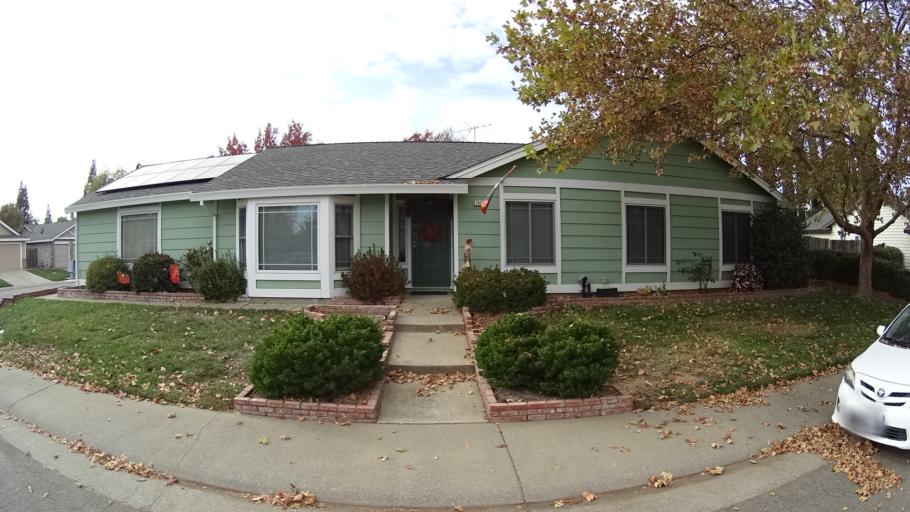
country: US
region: California
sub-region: Sacramento County
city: Citrus Heights
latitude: 38.7055
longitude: -121.2647
